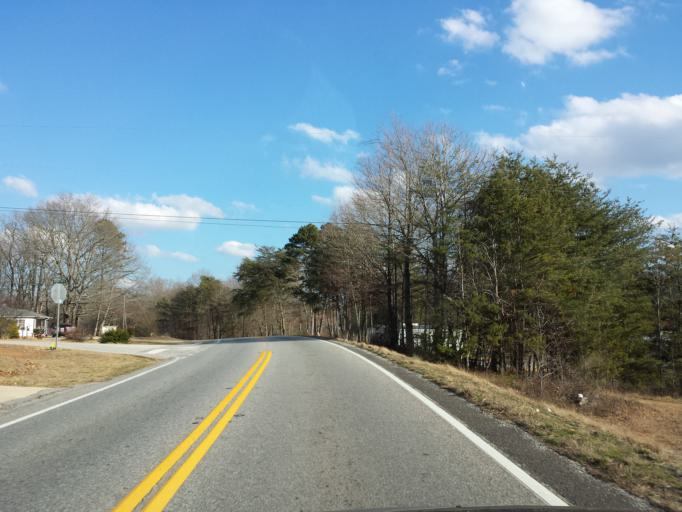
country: US
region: Georgia
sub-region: White County
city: Cleveland
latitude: 34.5359
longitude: -83.8159
